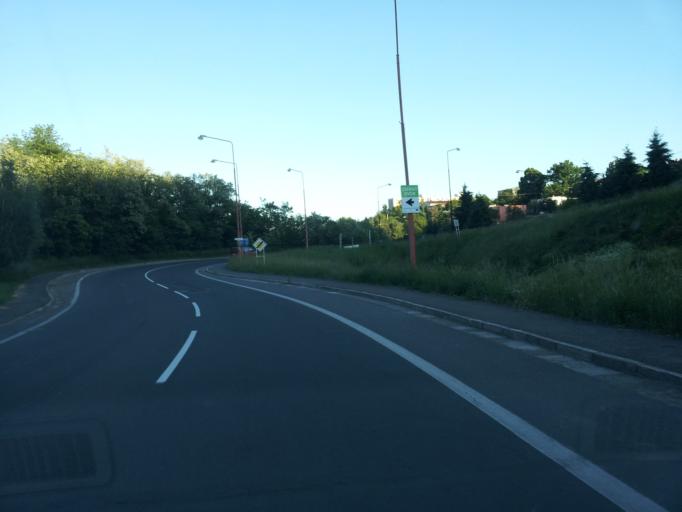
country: SK
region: Banskobystricky
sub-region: Okres Banska Bystrica
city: Banska Stiavnica
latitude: 48.4447
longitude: 18.9108
